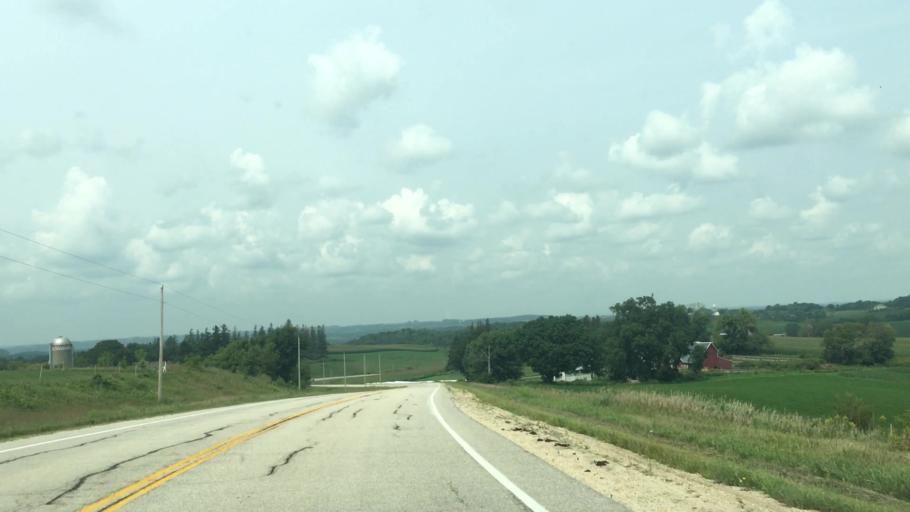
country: US
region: Minnesota
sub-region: Fillmore County
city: Preston
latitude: 43.6900
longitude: -91.9461
